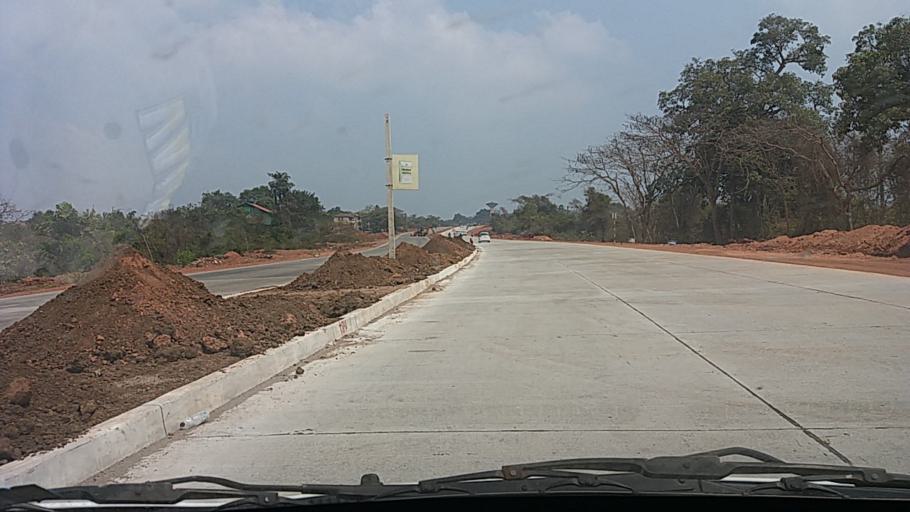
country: IN
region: Goa
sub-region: North Goa
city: Bambolim
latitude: 15.4570
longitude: 73.8661
